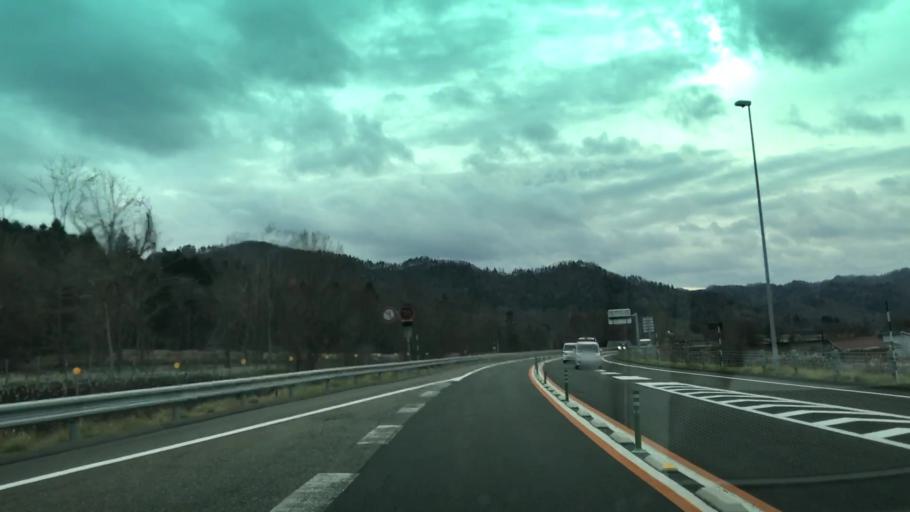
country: JP
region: Hokkaido
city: Iwamizawa
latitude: 42.9191
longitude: 142.0357
